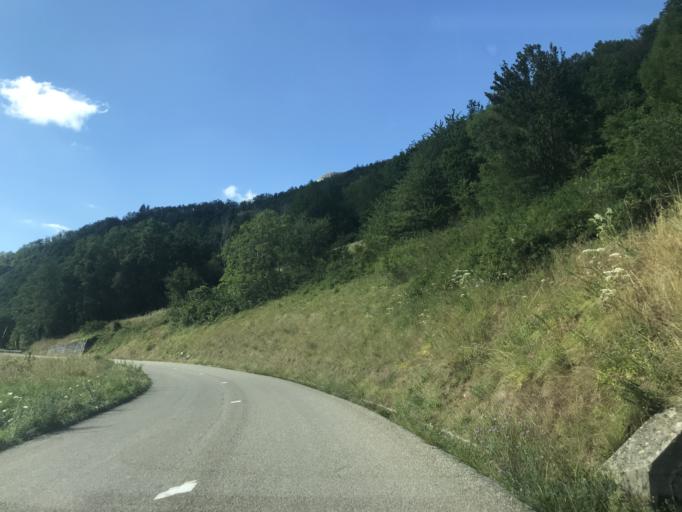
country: FR
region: Rhone-Alpes
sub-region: Departement de la Savoie
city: Brison-Saint-Innocent
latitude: 45.7120
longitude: 5.8284
